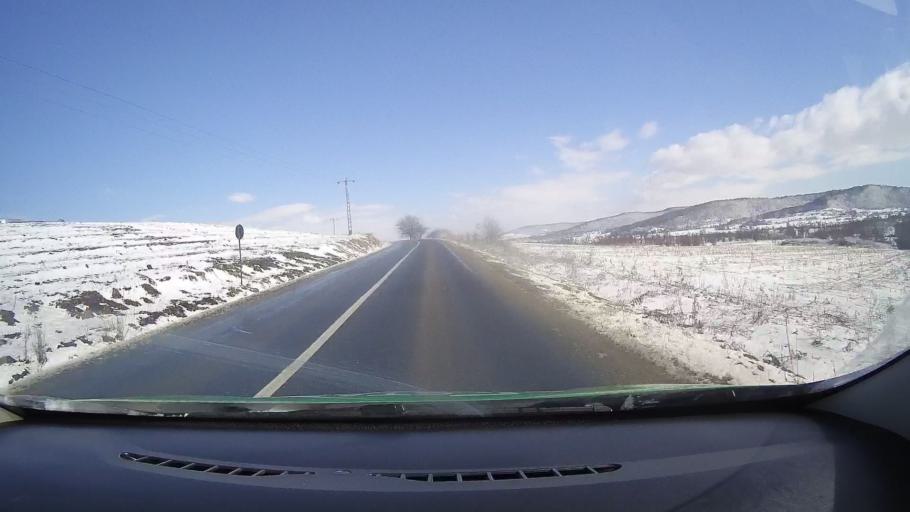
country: RO
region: Sibiu
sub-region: Comuna Rosia
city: Rosia
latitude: 45.8171
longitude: 24.3737
